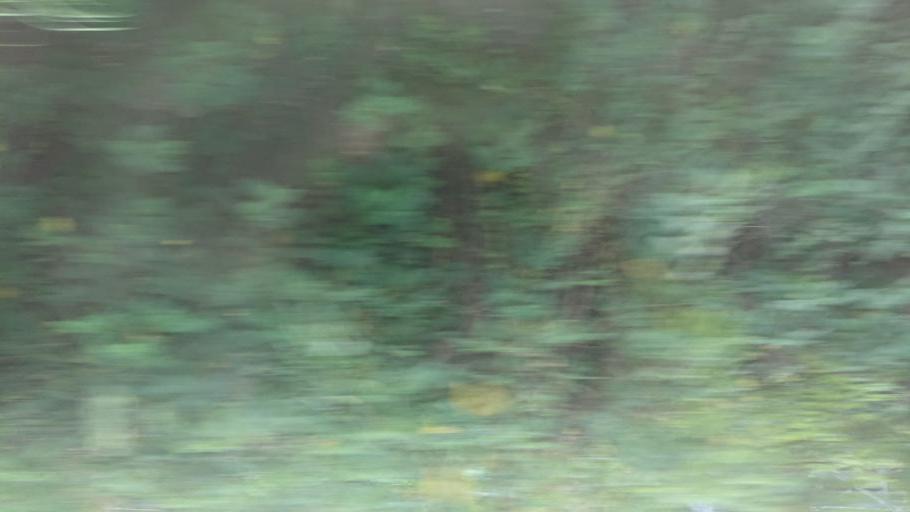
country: TW
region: Taiwan
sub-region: Hualien
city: Hualian
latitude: 23.9705
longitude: 121.5866
